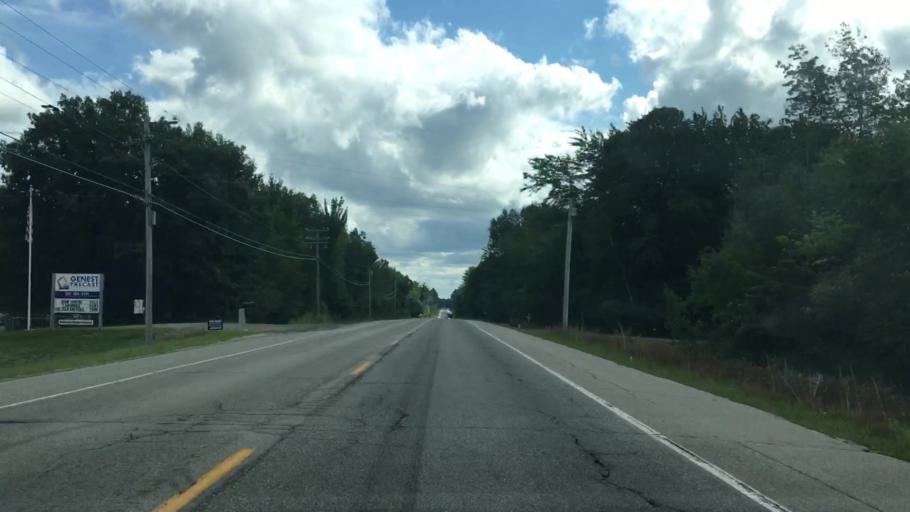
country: US
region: Maine
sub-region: York County
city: South Sanford
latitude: 43.3951
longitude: -70.7393
